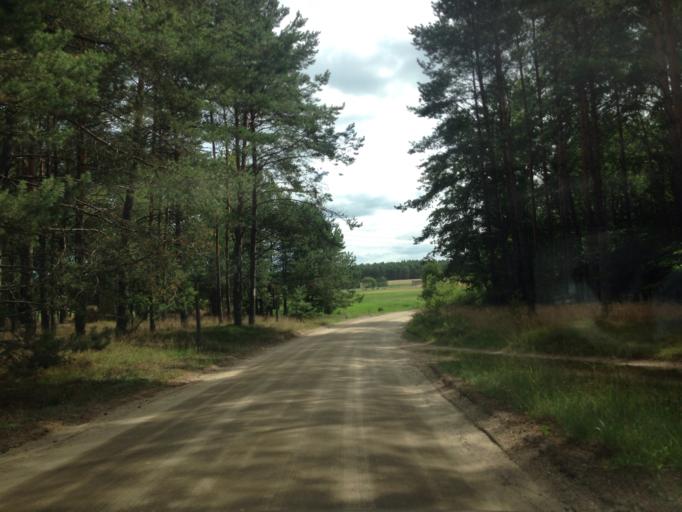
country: PL
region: Pomeranian Voivodeship
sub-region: Powiat koscierski
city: Lipusz
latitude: 54.0746
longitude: 17.6928
